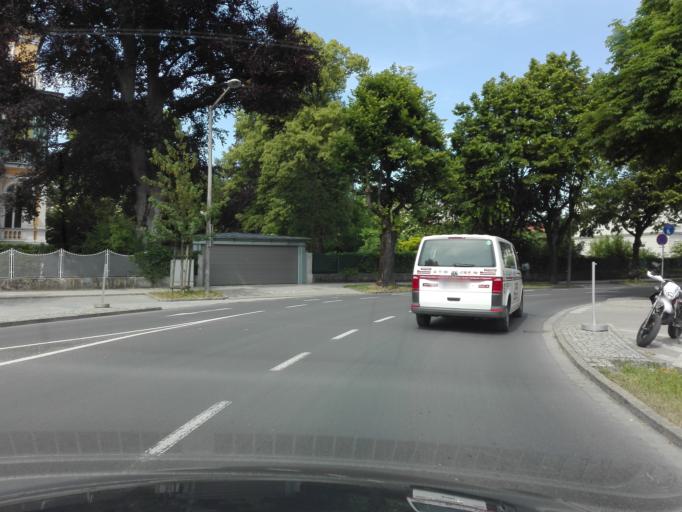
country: AT
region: Upper Austria
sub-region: Wels-Land
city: Thalheim bei Wels
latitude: 48.1545
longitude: 14.0230
